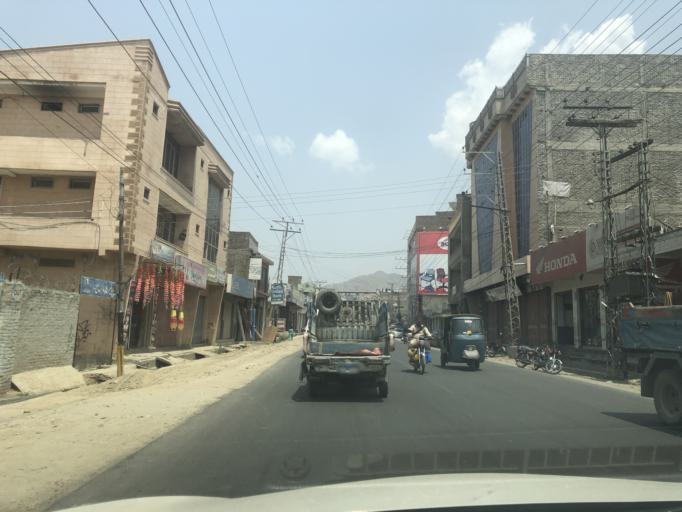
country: PK
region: Khyber Pakhtunkhwa
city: Mingora
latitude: 34.7702
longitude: 72.3432
